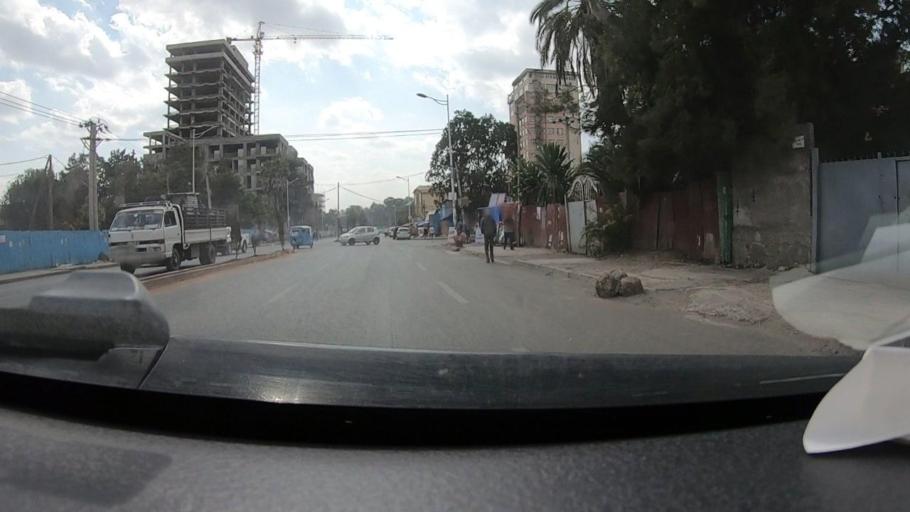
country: ET
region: Adis Abeba
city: Addis Ababa
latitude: 9.0450
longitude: 38.7653
